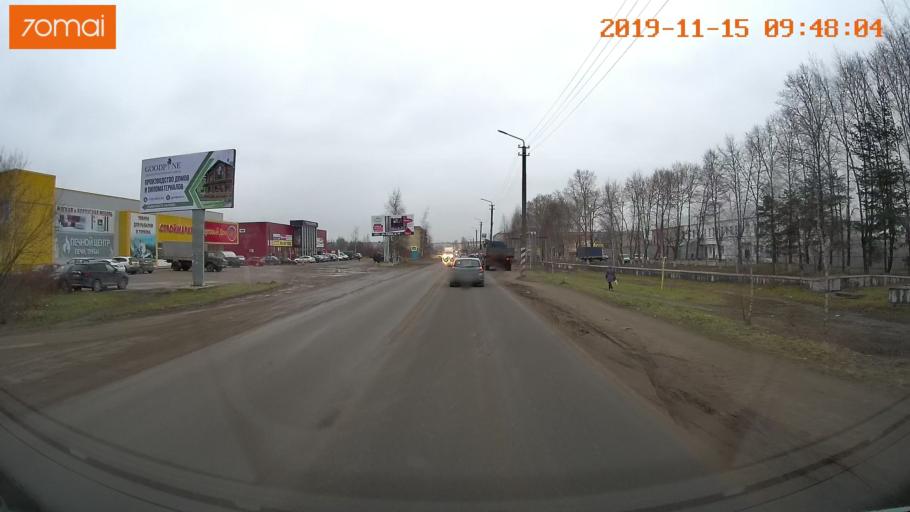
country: RU
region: Vologda
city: Sheksna
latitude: 59.2207
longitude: 38.5119
